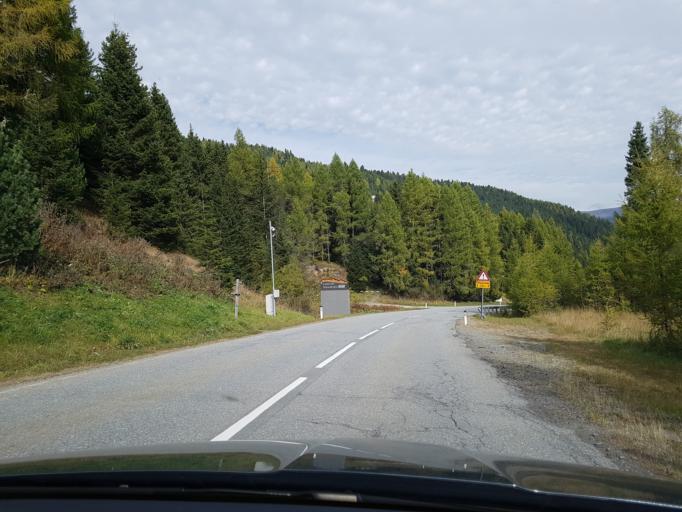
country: AT
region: Carinthia
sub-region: Politischer Bezirk Spittal an der Drau
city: Kleinkirchheim
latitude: 46.9310
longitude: 13.8727
